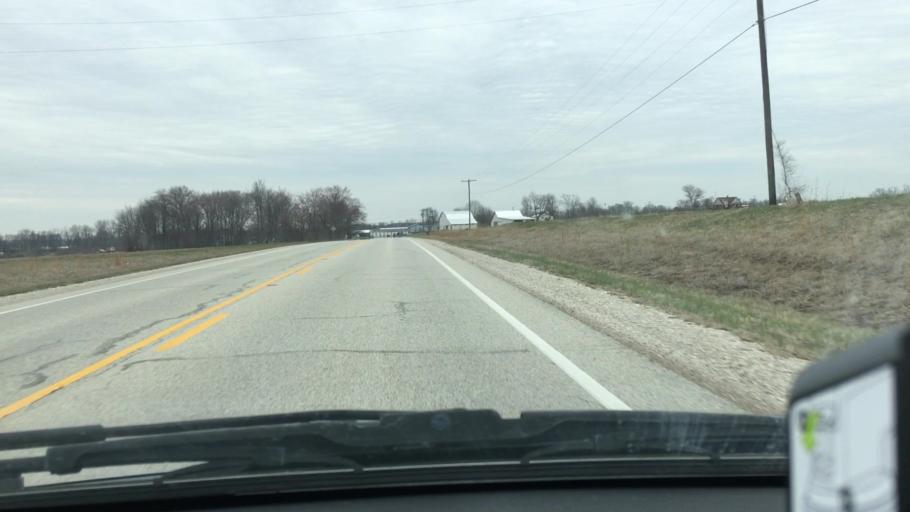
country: US
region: Indiana
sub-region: Greene County
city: Bloomfield
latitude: 39.0203
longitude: -87.0151
